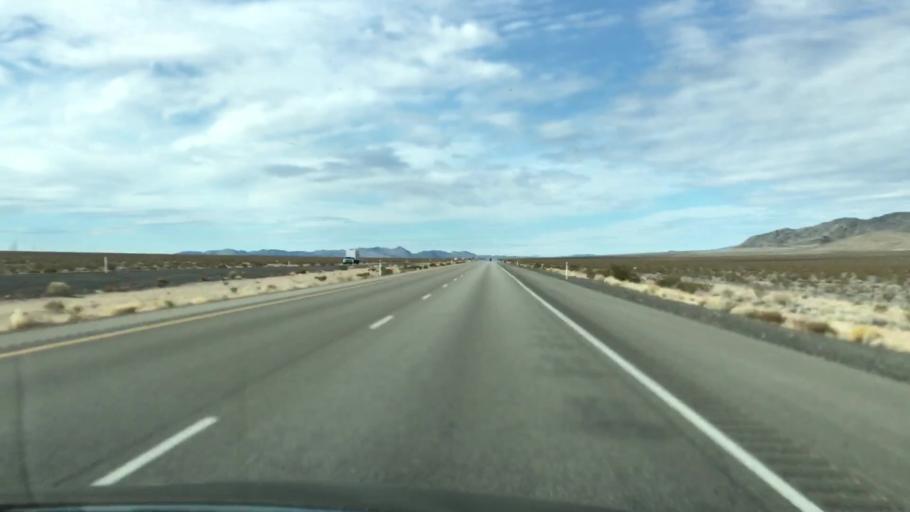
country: US
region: Nevada
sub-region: Nye County
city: Pahrump
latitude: 36.5885
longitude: -115.9250
